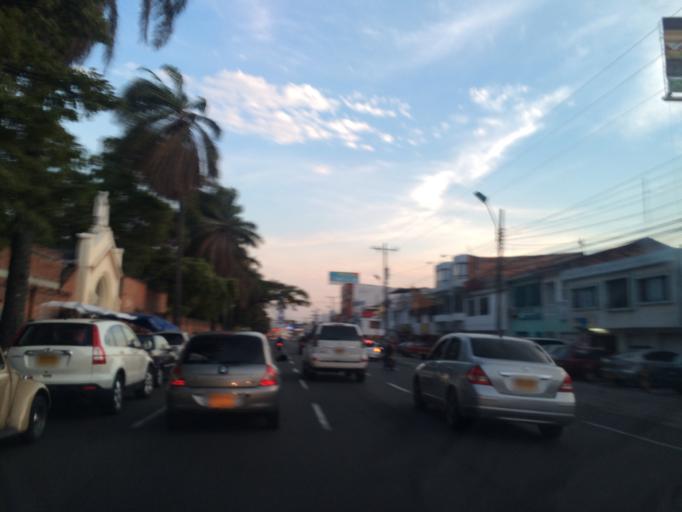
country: CO
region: Valle del Cauca
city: Cali
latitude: 3.4314
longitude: -76.5389
